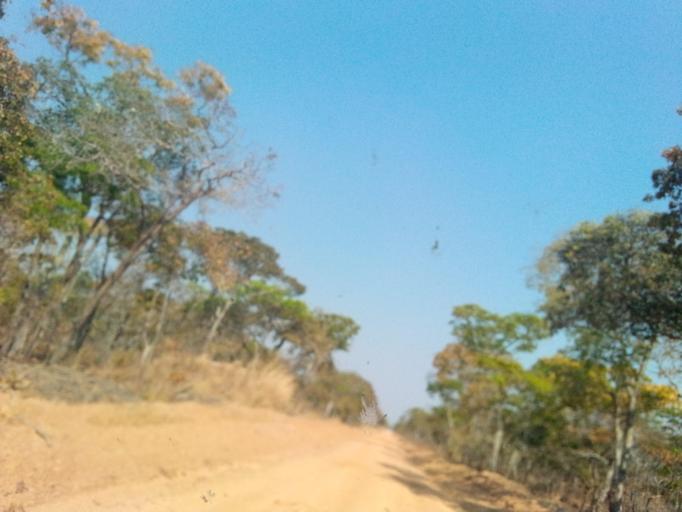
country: ZM
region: Northern
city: Mpika
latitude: -12.2302
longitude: 30.9207
